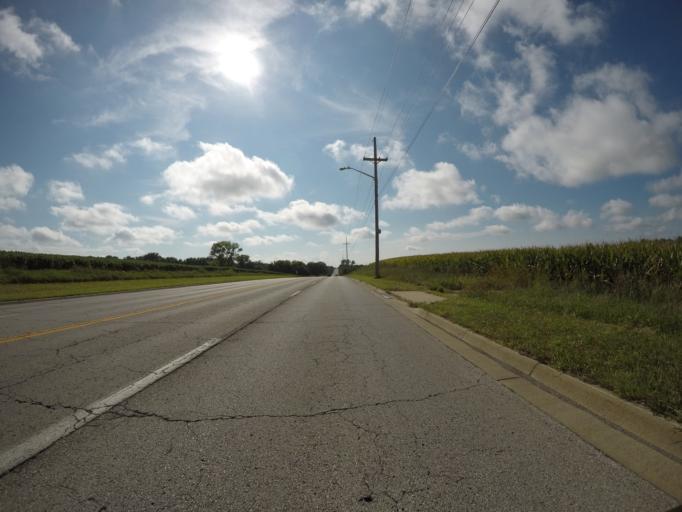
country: US
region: Kansas
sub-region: Leavenworth County
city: Basehor
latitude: 39.1287
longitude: -94.8786
